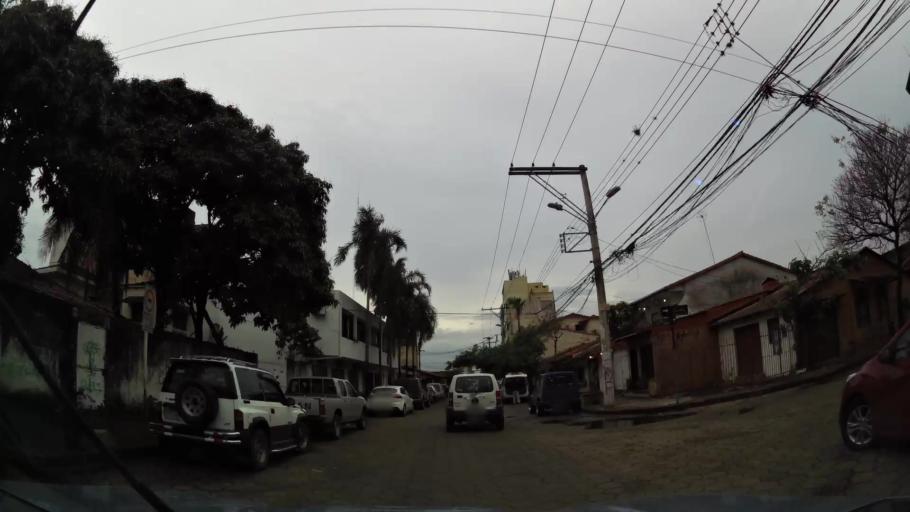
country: BO
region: Santa Cruz
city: Santa Cruz de la Sierra
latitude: -17.7862
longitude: -63.1740
